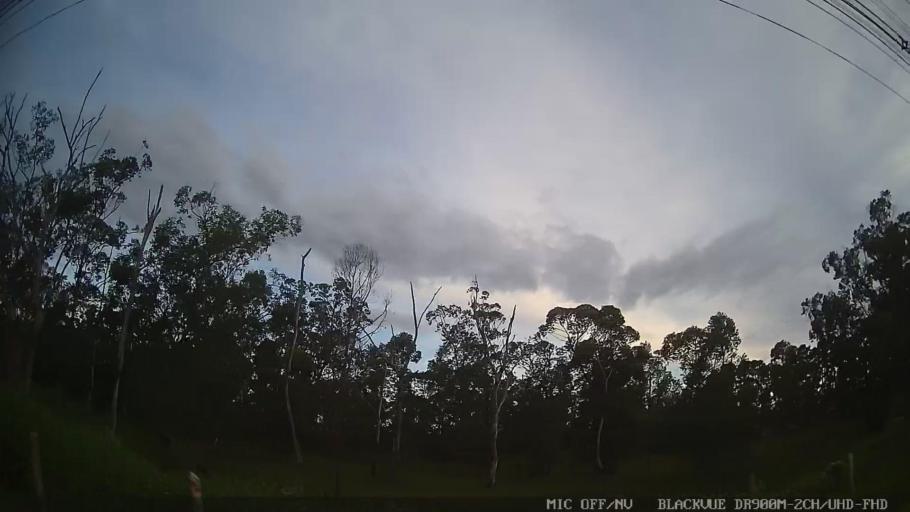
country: BR
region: Sao Paulo
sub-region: Suzano
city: Suzano
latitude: -23.5214
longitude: -46.3012
